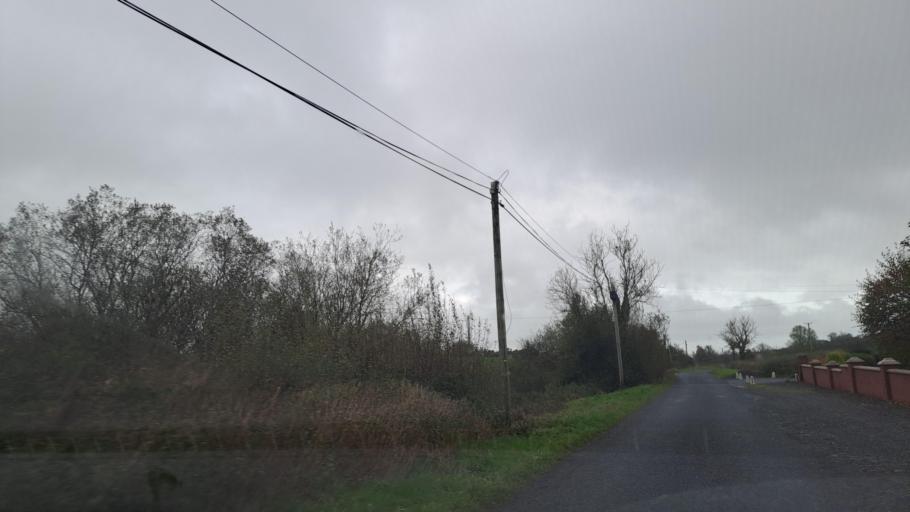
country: IE
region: Ulster
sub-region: An Cabhan
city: Kingscourt
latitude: 53.9626
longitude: -6.8748
